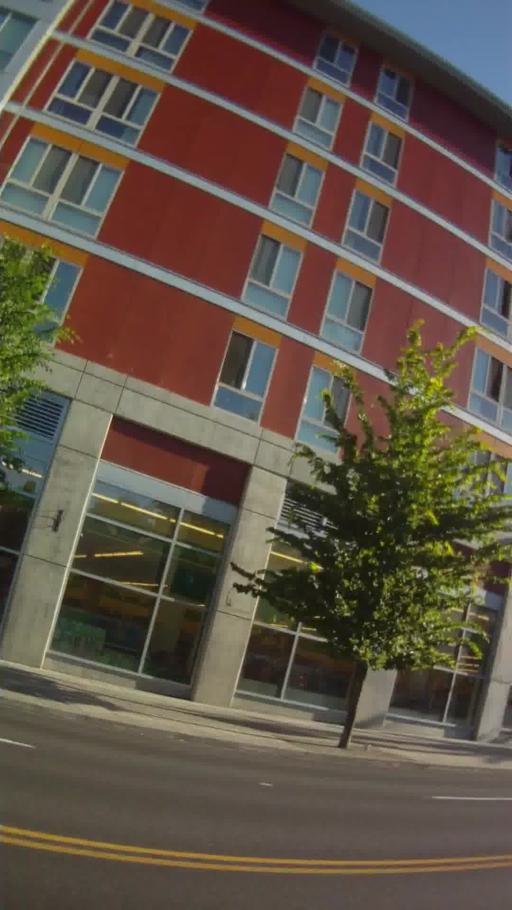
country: US
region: Oregon
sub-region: Multnomah County
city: Portland
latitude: 45.5231
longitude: -122.6910
